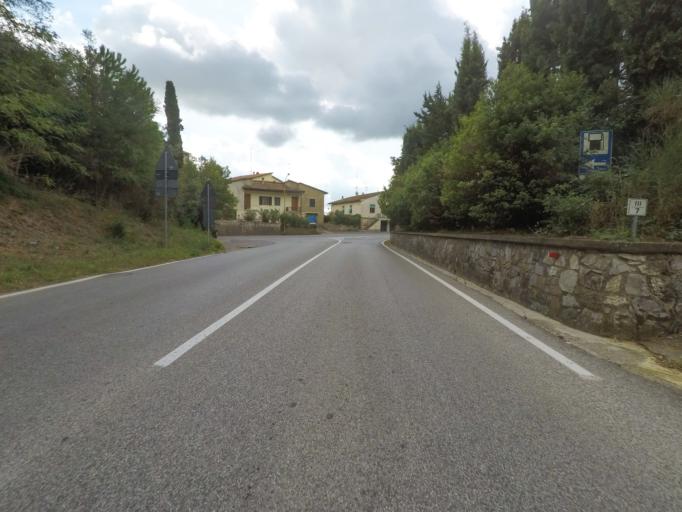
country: IT
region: Tuscany
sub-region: Provincia di Siena
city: Montepulciano
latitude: 43.1105
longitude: 11.7893
